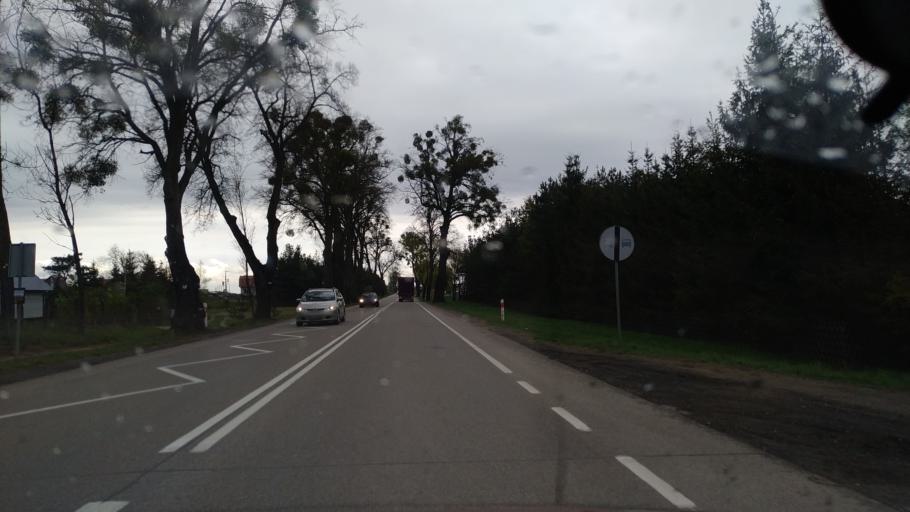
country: PL
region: Pomeranian Voivodeship
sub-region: Powiat starogardzki
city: Kaliska
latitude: 53.9134
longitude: 18.2686
